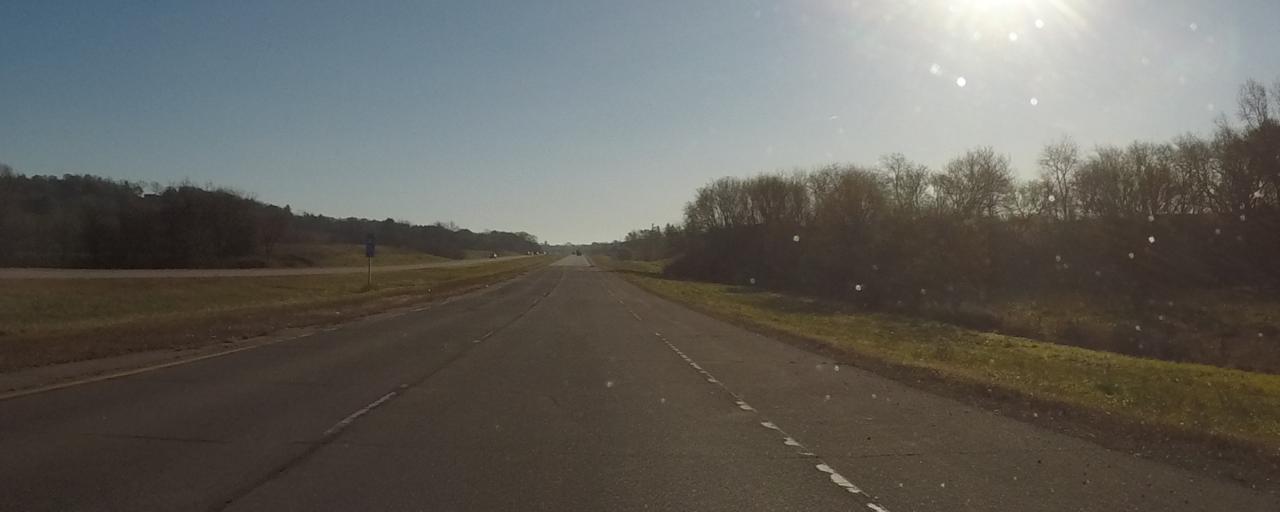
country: US
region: Wisconsin
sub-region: Dane County
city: Cottage Grove
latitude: 43.0379
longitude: -89.2361
